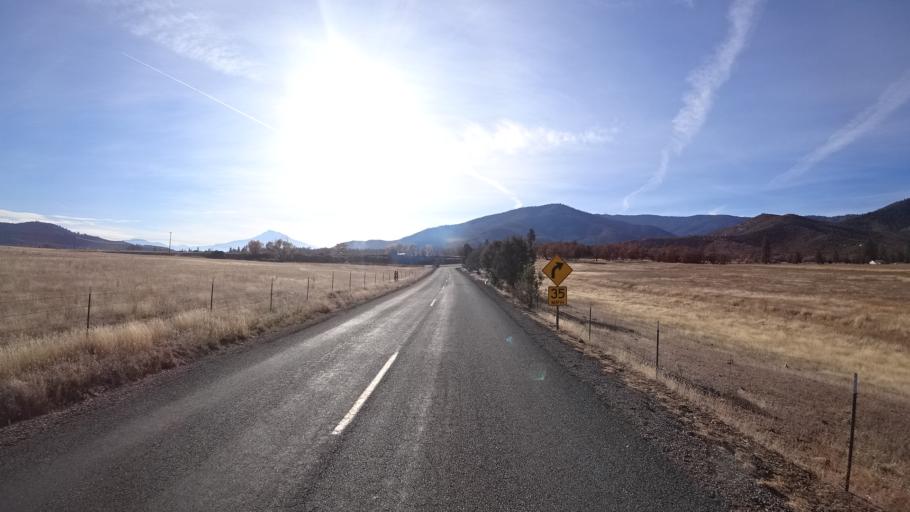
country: US
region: California
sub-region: Siskiyou County
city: Yreka
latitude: 41.6740
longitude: -122.6240
